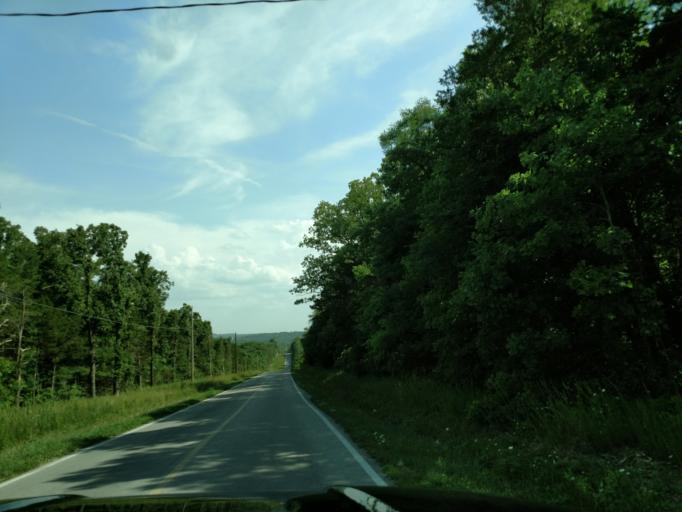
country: US
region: Missouri
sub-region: Barry County
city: Shell Knob
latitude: 36.6095
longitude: -93.5811
